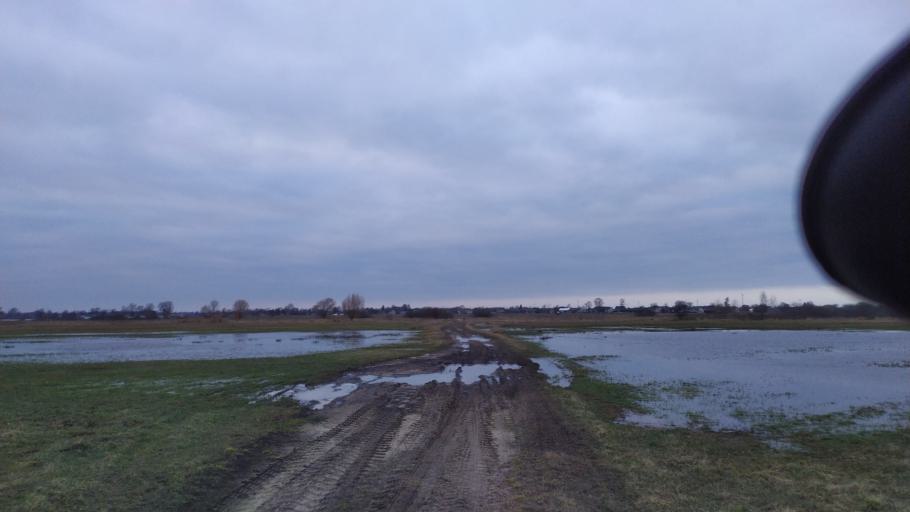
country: PL
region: Lublin Voivodeship
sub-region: Powiat lubartowski
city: Abramow
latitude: 51.4323
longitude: 22.2949
